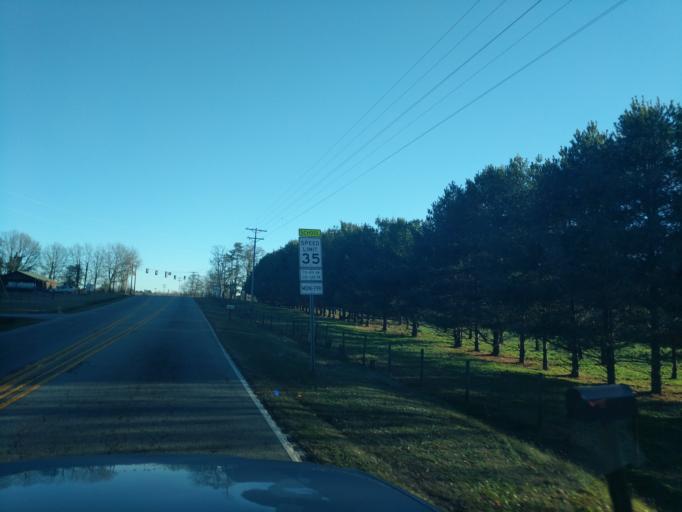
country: US
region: South Carolina
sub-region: Oconee County
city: Westminster
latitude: 34.6264
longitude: -83.0556
